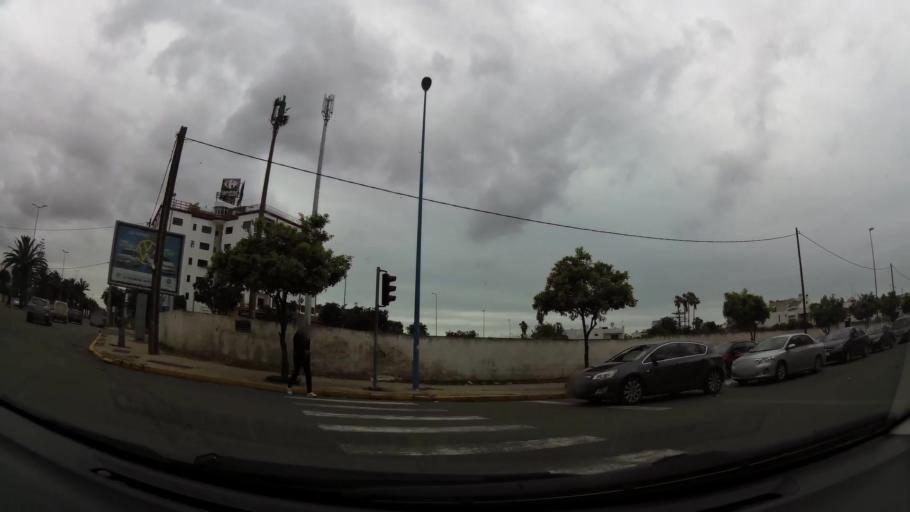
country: MA
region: Grand Casablanca
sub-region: Casablanca
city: Casablanca
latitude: 33.5908
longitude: -7.6453
